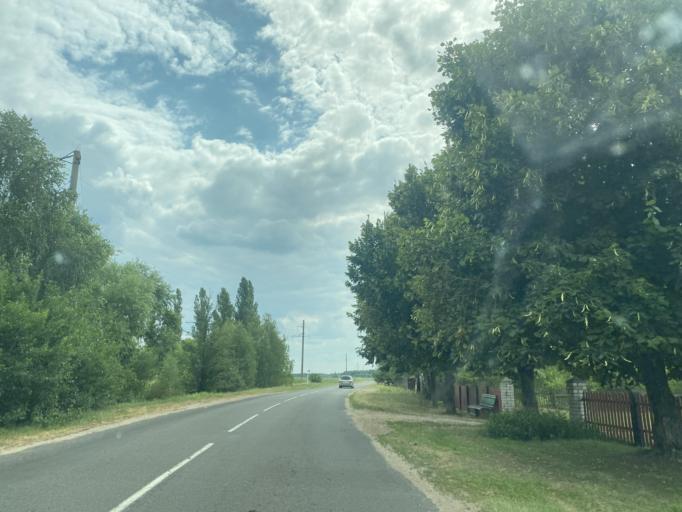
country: BY
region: Brest
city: Ivanava
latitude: 52.3485
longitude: 25.6290
